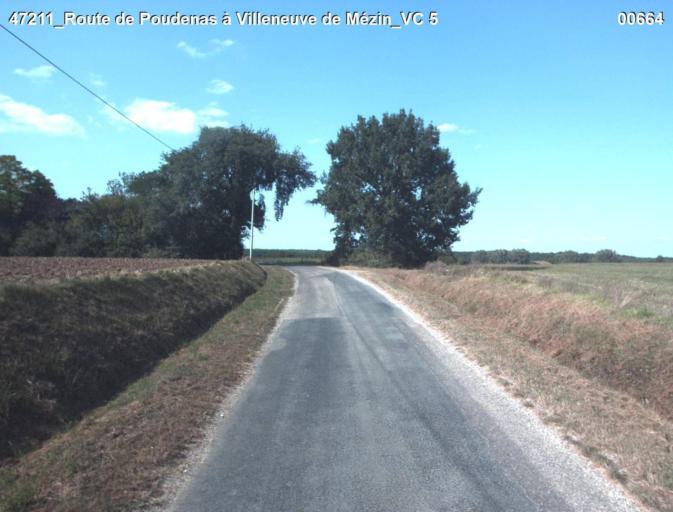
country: FR
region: Aquitaine
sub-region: Departement du Lot-et-Garonne
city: Mezin
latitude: 44.0399
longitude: 0.2190
